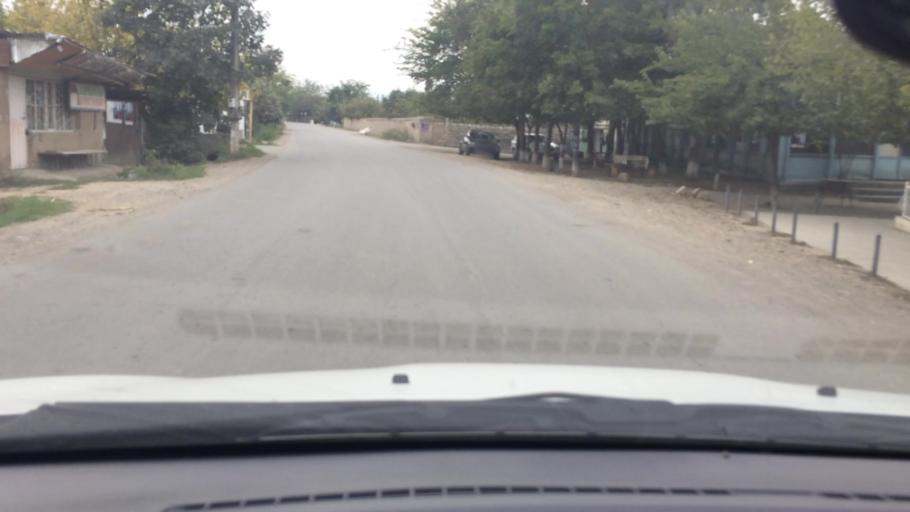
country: AM
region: Tavush
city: Bagratashen
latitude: 41.3408
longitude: 44.9294
